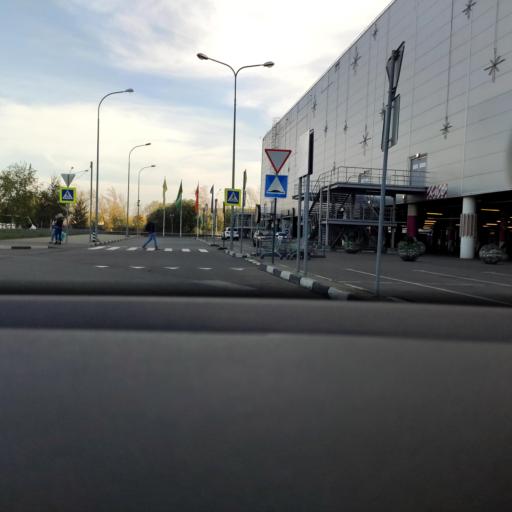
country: RU
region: Moskovskaya
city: Kotel'niki
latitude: 55.6594
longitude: 37.8464
